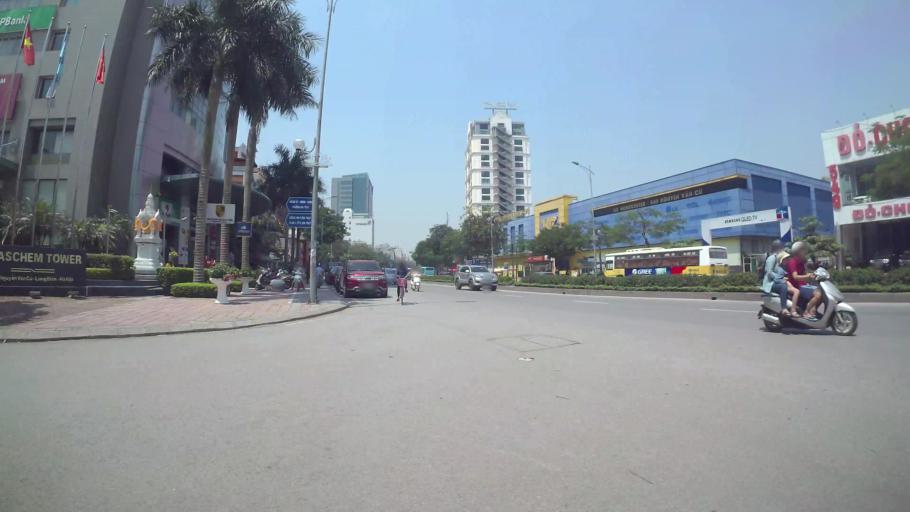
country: VN
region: Ha Noi
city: Hoan Kiem
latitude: 21.0504
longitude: 105.8840
